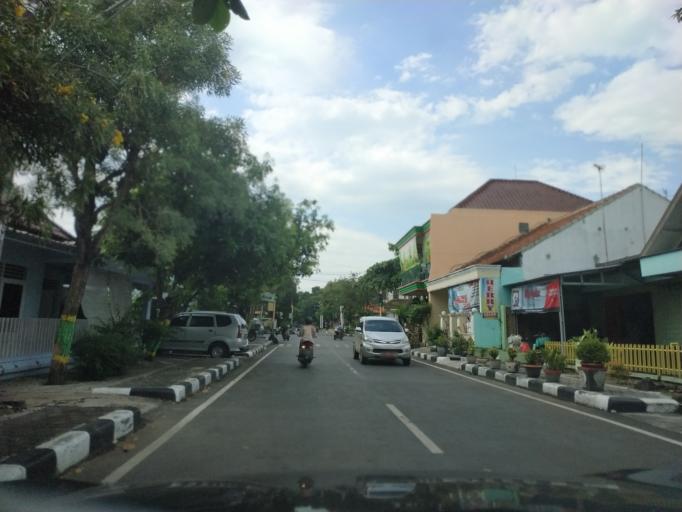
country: ID
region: Central Java
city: Pati
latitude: -6.7551
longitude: 111.0327
